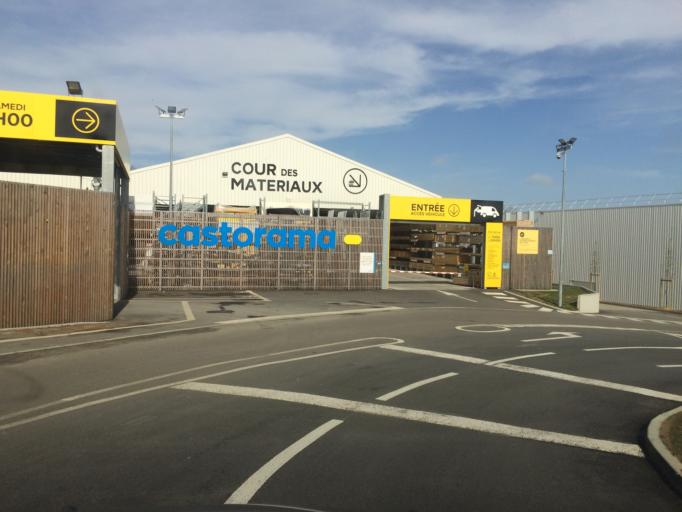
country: FR
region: Pays de la Loire
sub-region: Departement de la Loire-Atlantique
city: Saint-Andre-des-Eaux
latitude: 47.2595
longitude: -2.2672
